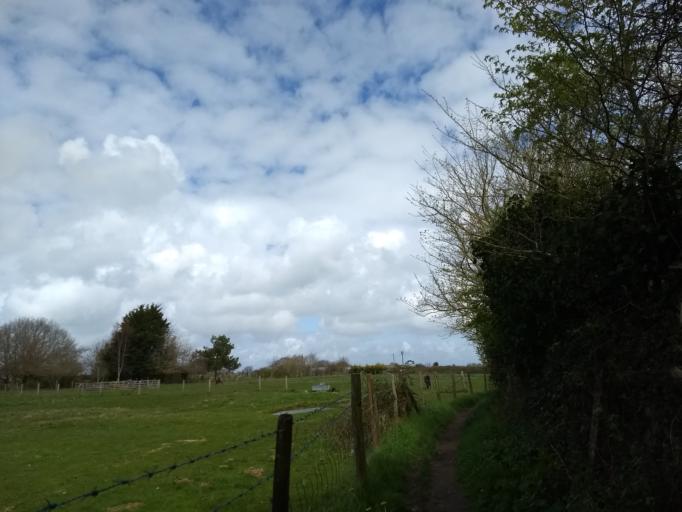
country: GB
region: England
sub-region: Isle of Wight
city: East Cowes
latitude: 50.7315
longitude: -1.2344
